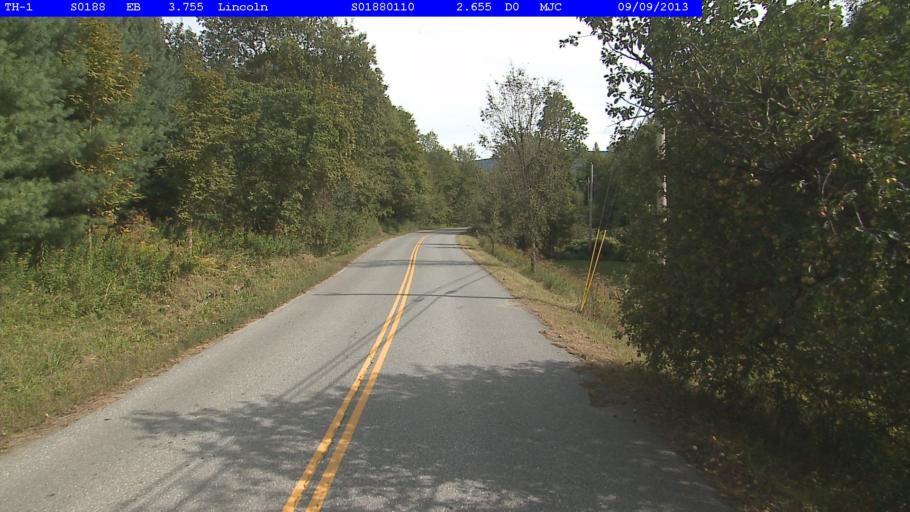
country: US
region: Vermont
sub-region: Addison County
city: Bristol
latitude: 44.1018
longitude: -72.9919
